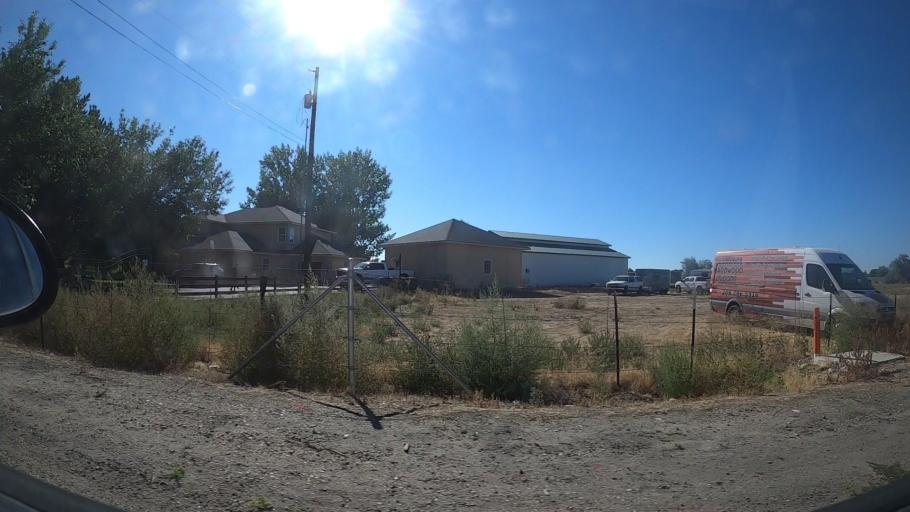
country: US
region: Idaho
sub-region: Canyon County
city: Nampa
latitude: 43.6040
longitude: -116.6134
